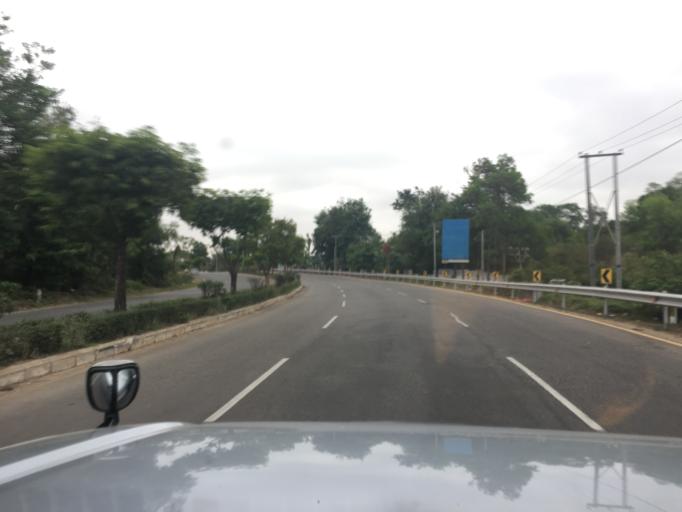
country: MM
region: Bago
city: Thanatpin
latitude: 17.2172
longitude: 96.4294
